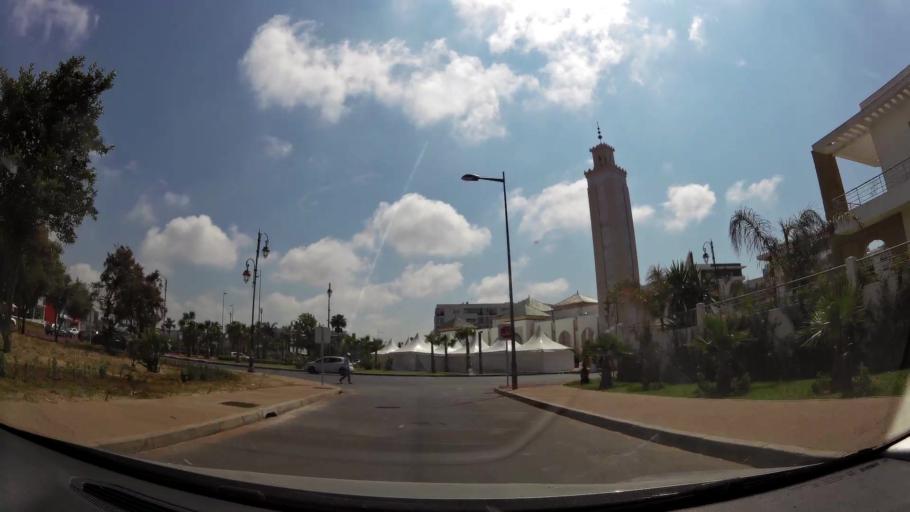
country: MA
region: Rabat-Sale-Zemmour-Zaer
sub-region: Skhirate-Temara
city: Temara
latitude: 33.9544
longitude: -6.8810
